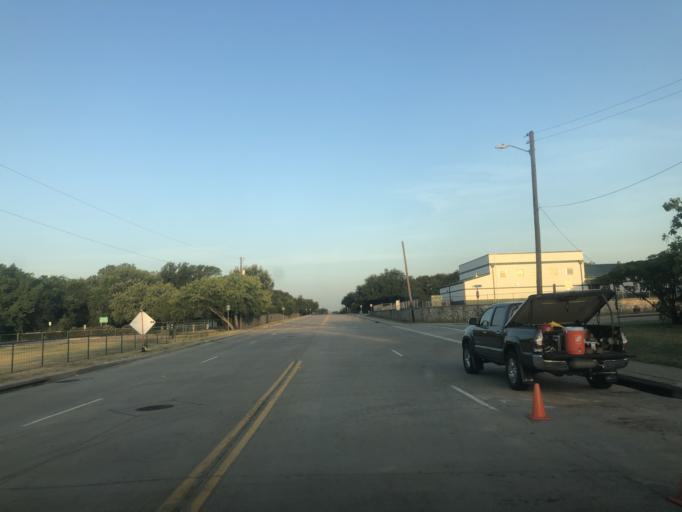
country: US
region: Texas
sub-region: Tarrant County
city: Lake Worth
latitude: 32.8103
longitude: -97.4367
